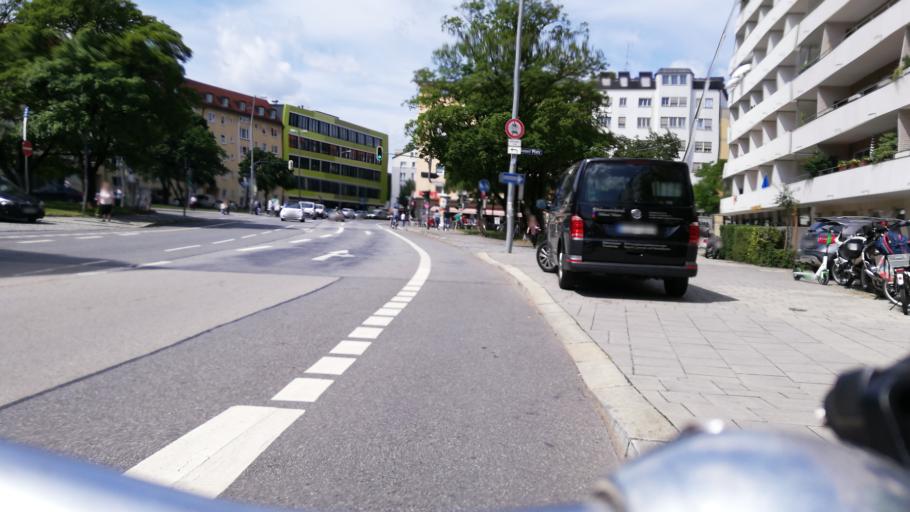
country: DE
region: Bavaria
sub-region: Upper Bavaria
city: Munich
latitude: 48.1671
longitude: 11.5795
